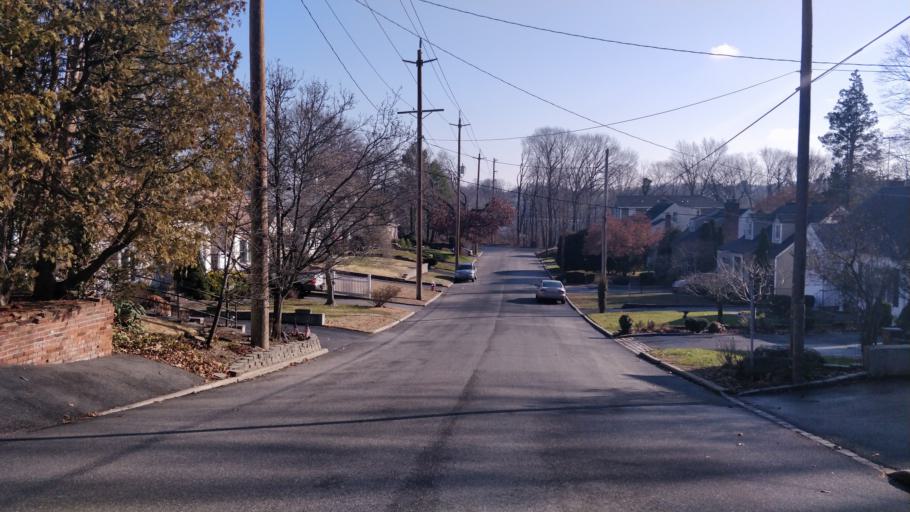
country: US
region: New York
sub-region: Nassau County
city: Glen Cove
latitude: 40.8583
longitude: -73.6261
